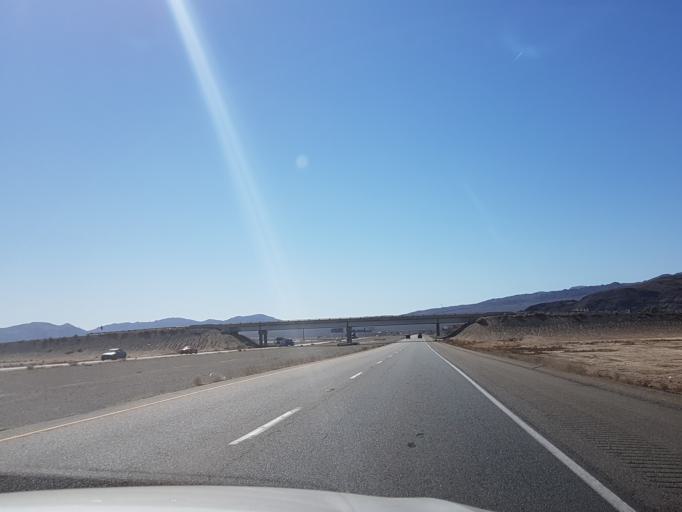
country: US
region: California
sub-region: San Bernardino County
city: Fort Irwin
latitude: 35.2648
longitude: -116.0714
